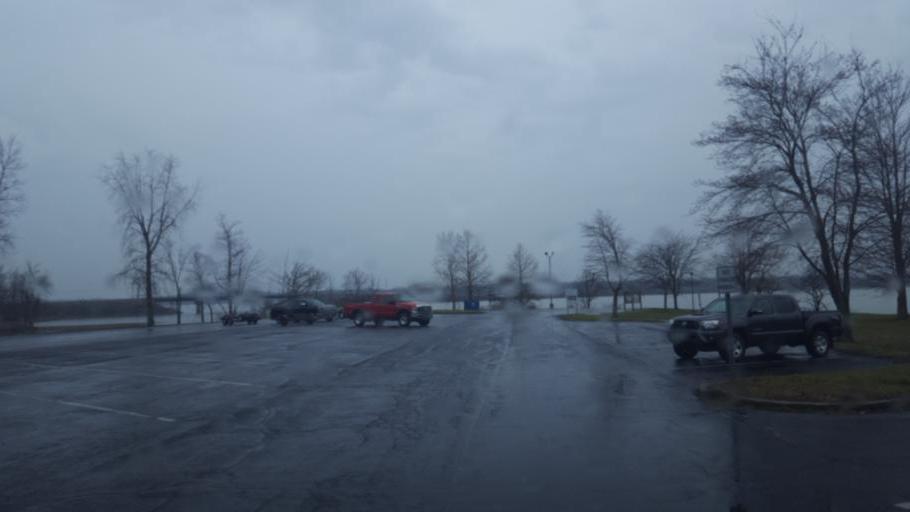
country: US
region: Ohio
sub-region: Delaware County
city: Lewis Center
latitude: 40.2427
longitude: -82.9636
